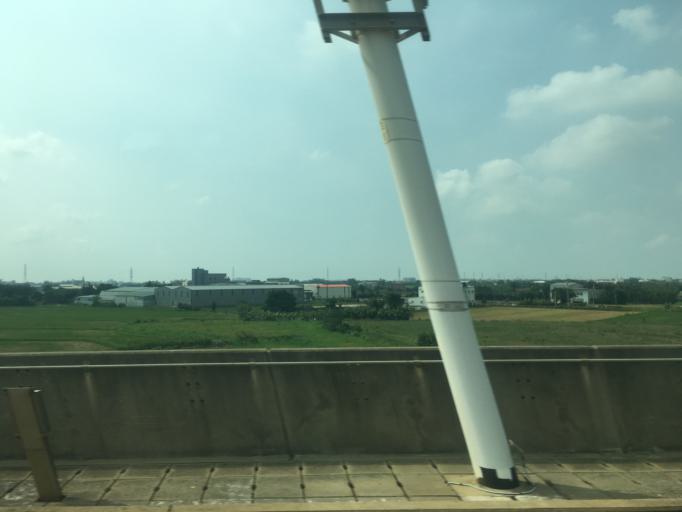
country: TW
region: Taiwan
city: Taoyuan City
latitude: 24.9491
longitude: 121.1353
